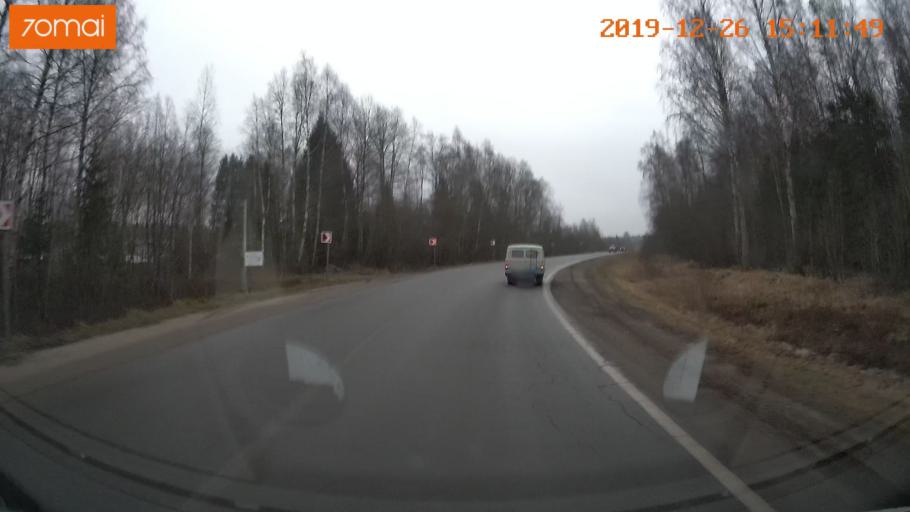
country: RU
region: Jaroslavl
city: Rybinsk
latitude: 58.1325
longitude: 38.8674
